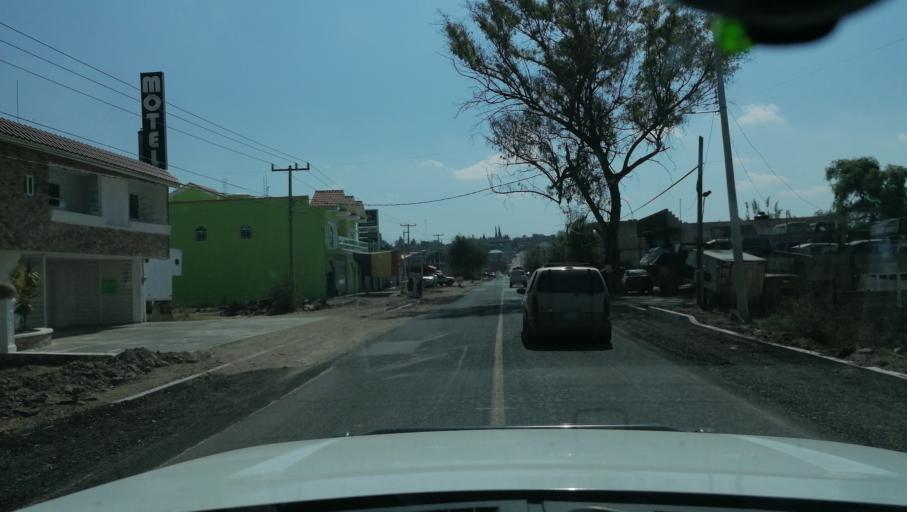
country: MX
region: Tlaxcala
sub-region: San Jeronimo Zacualpan
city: San Jeronimo Zacualpan
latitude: 19.2387
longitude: -98.2573
